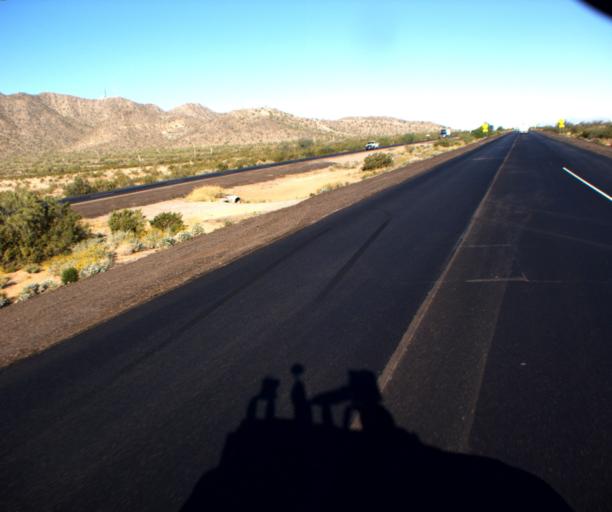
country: US
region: Arizona
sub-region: Pinal County
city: Arizona City
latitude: 32.8218
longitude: -111.6909
